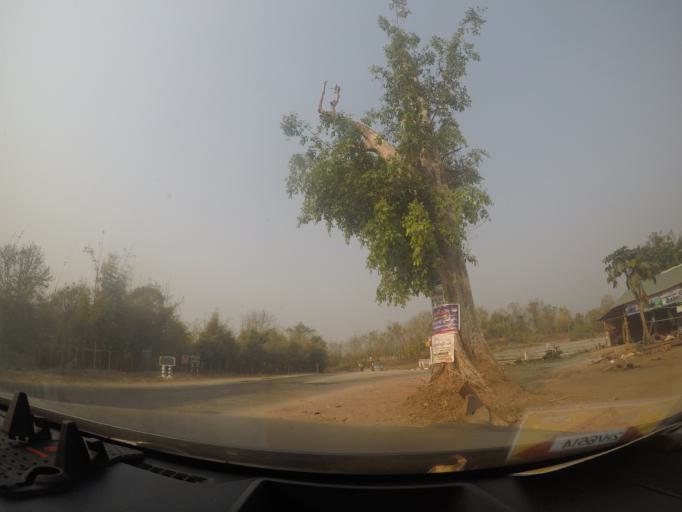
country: MM
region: Mandalay
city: Nay Pyi Taw
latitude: 19.9278
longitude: 95.9842
